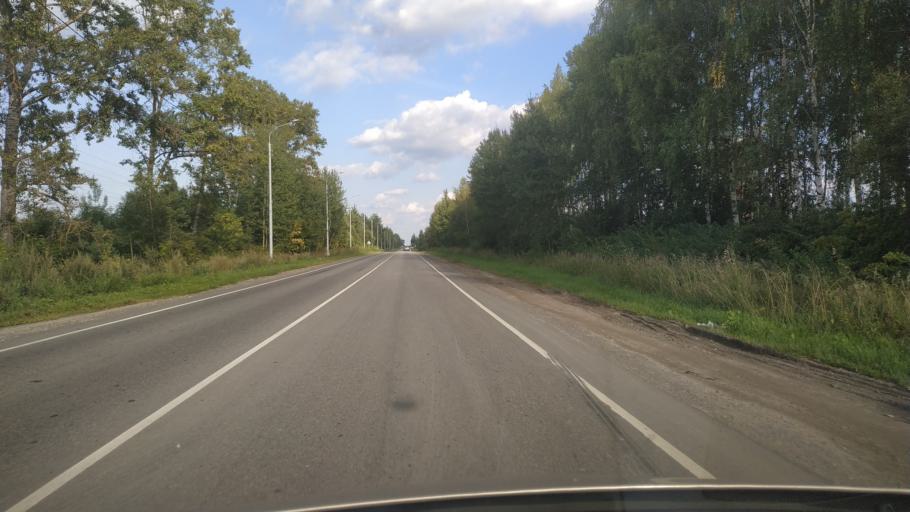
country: RU
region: Moskovskaya
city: Vereya
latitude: 55.7086
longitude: 39.0943
